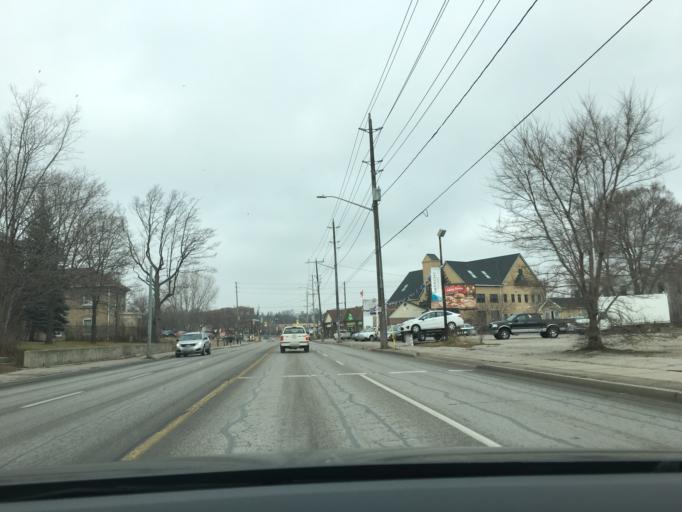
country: CA
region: Ontario
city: Barrie
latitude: 44.3845
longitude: -79.6939
